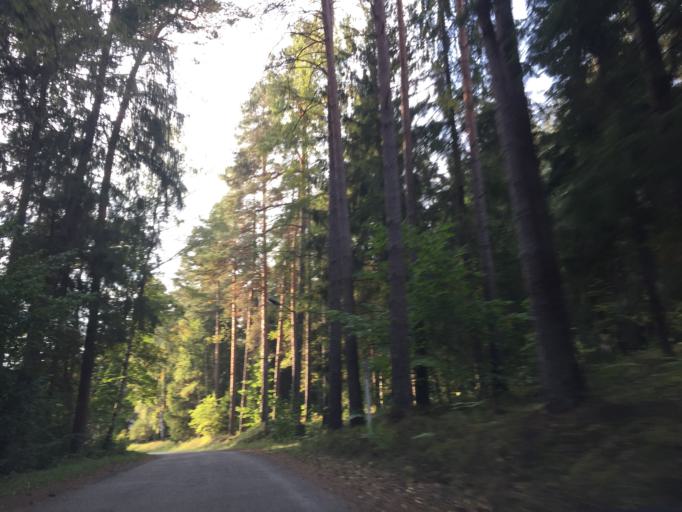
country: LV
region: Baldone
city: Baldone
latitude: 56.7744
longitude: 24.4131
